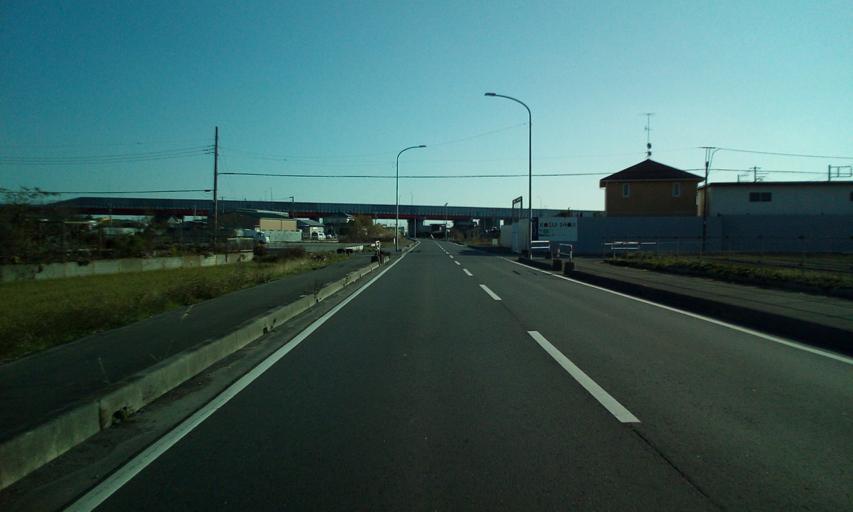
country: JP
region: Chiba
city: Nagareyama
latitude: 35.8765
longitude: 139.8885
